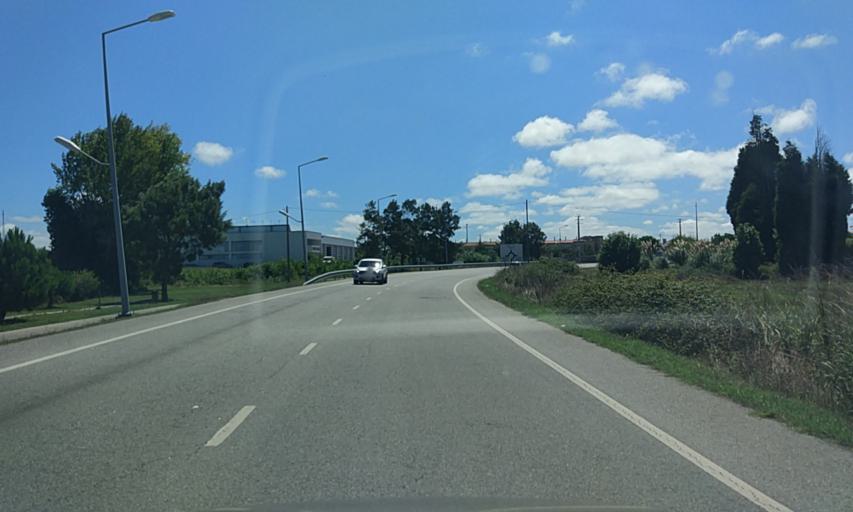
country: PT
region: Aveiro
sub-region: Ilhavo
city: Ilhavo
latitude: 40.6014
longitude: -8.6787
